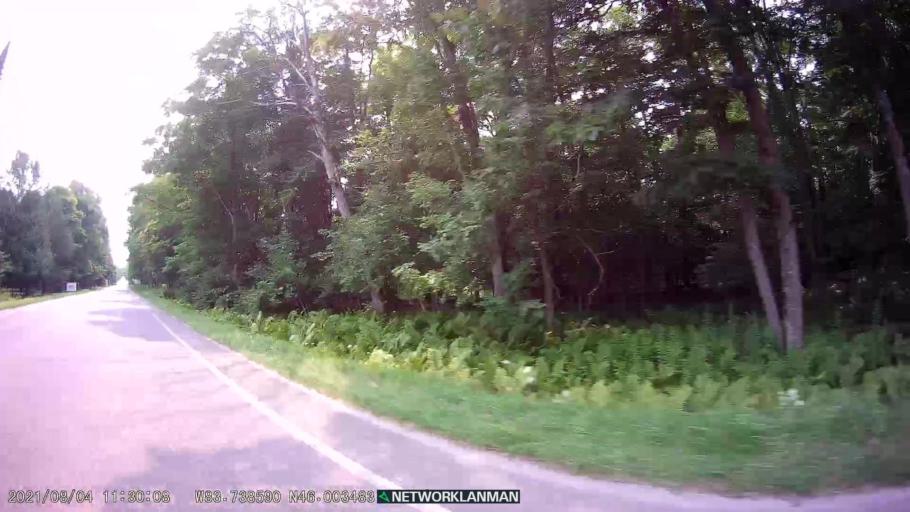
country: CA
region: Ontario
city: Thessalon
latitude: 46.0031
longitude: -83.7383
